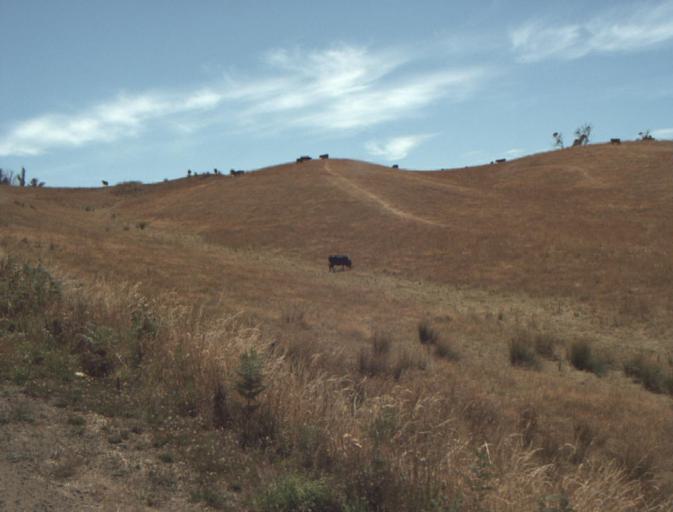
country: AU
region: Tasmania
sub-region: Launceston
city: Mayfield
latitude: -41.2504
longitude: 147.1341
